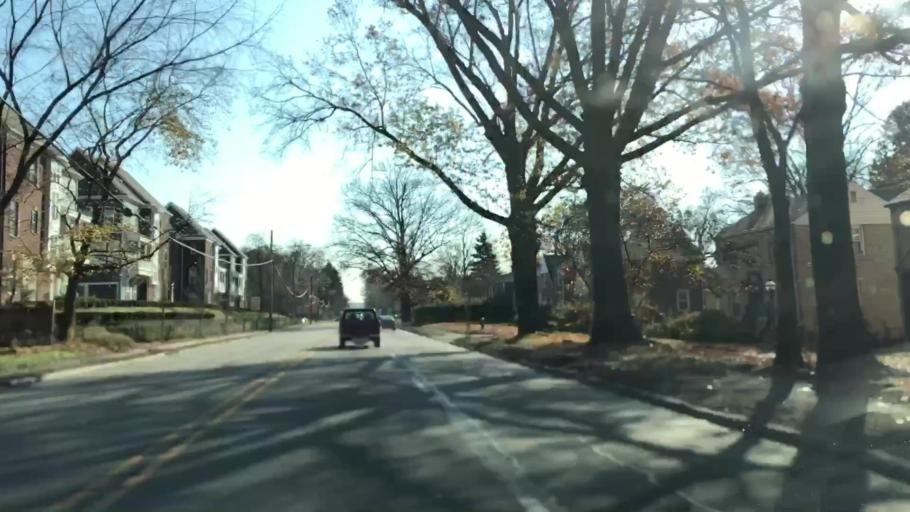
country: US
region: Pennsylvania
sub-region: Allegheny County
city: Sewickley
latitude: 40.5336
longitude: -80.1784
